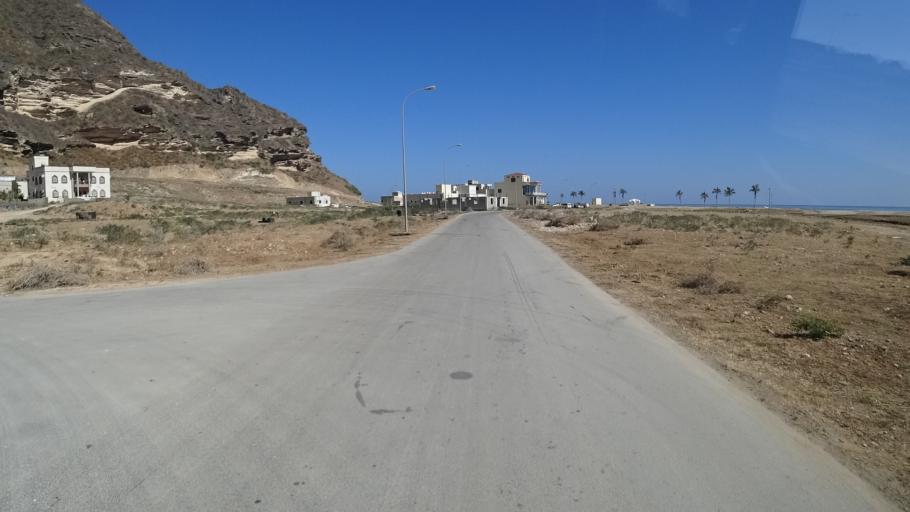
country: YE
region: Al Mahrah
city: Hawf
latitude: 16.7488
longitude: 53.4251
